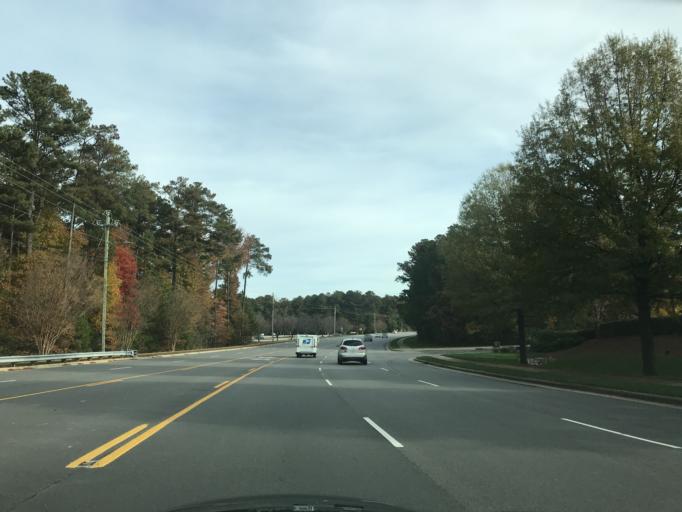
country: US
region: North Carolina
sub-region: Wake County
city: West Raleigh
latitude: 35.9007
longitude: -78.6510
